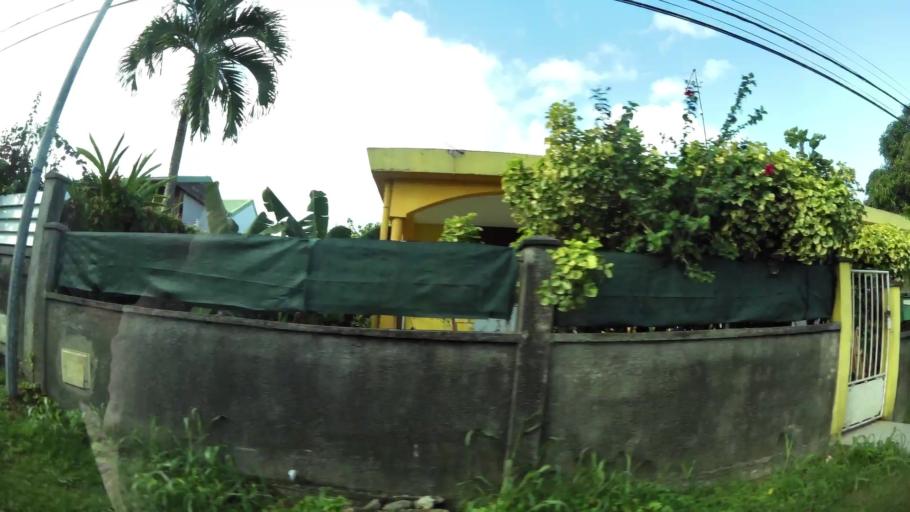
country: GP
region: Guadeloupe
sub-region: Guadeloupe
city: Les Abymes
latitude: 16.2543
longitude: -61.5129
